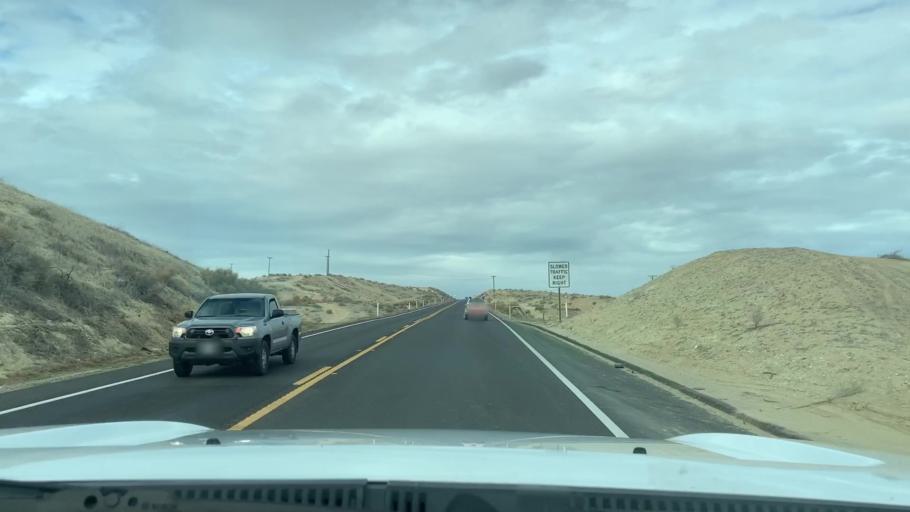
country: US
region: California
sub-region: Kern County
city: Maricopa
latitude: 35.0993
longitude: -119.4141
